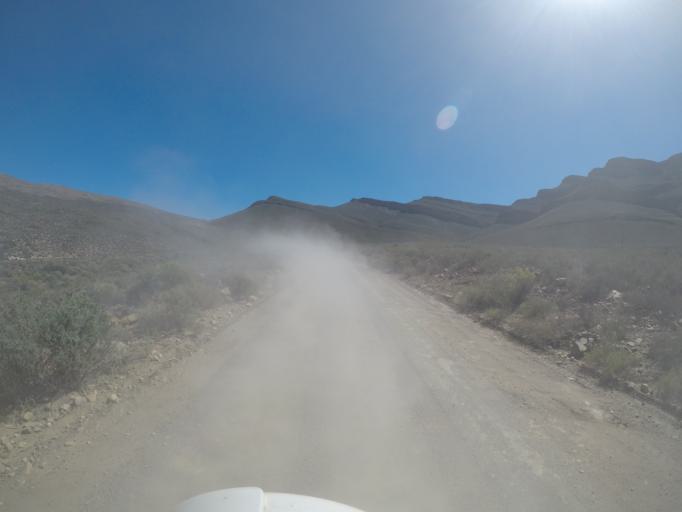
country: ZA
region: Western Cape
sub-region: West Coast District Municipality
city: Clanwilliam
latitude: -32.6239
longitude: 19.3878
